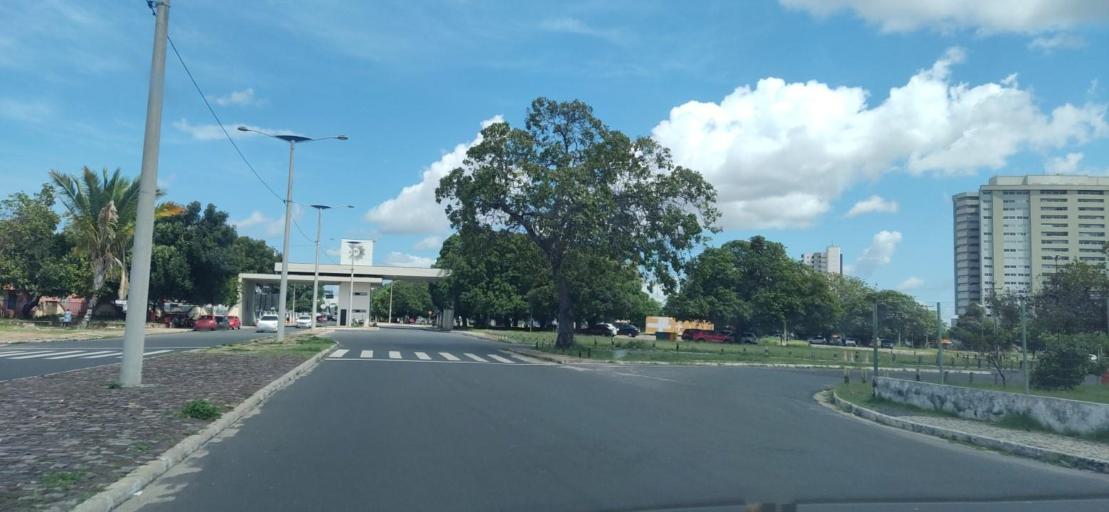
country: BR
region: Piaui
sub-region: Teresina
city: Teresina
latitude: -5.0605
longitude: -42.7952
